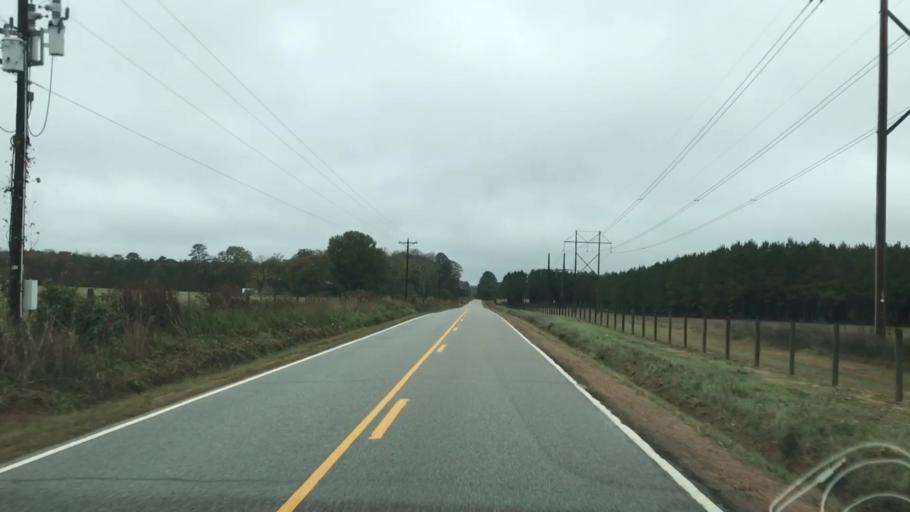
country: US
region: South Carolina
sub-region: Laurens County
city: Joanna
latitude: 34.3242
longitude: -81.9222
